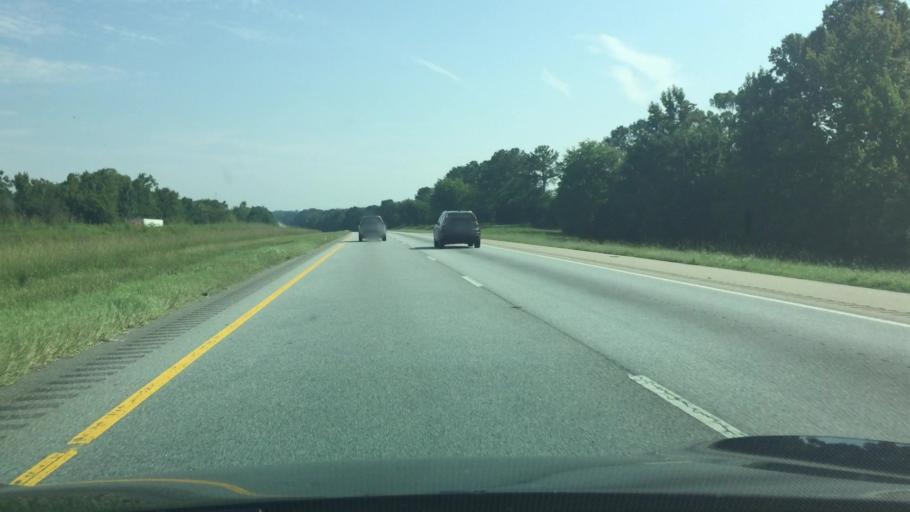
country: US
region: Alabama
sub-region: Lowndes County
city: Fort Deposit
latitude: 32.0595
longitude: -86.4909
